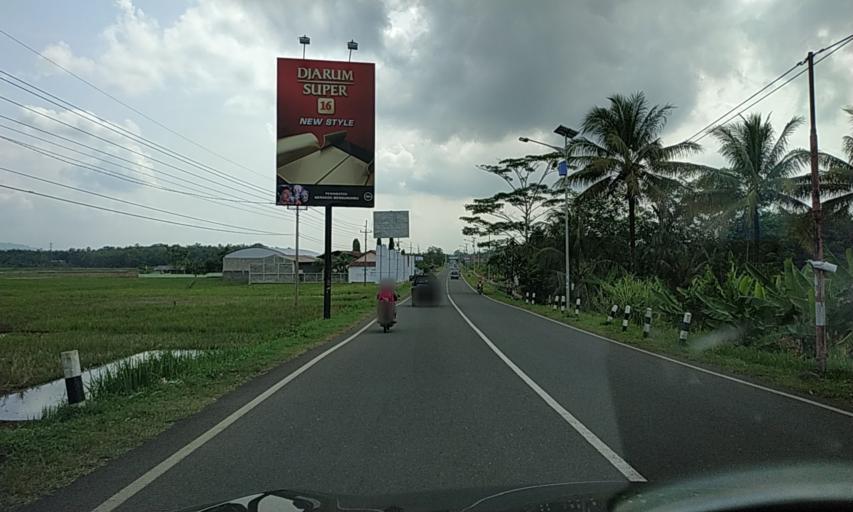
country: ID
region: Central Java
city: Wanareja
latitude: -7.3352
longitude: 108.6826
